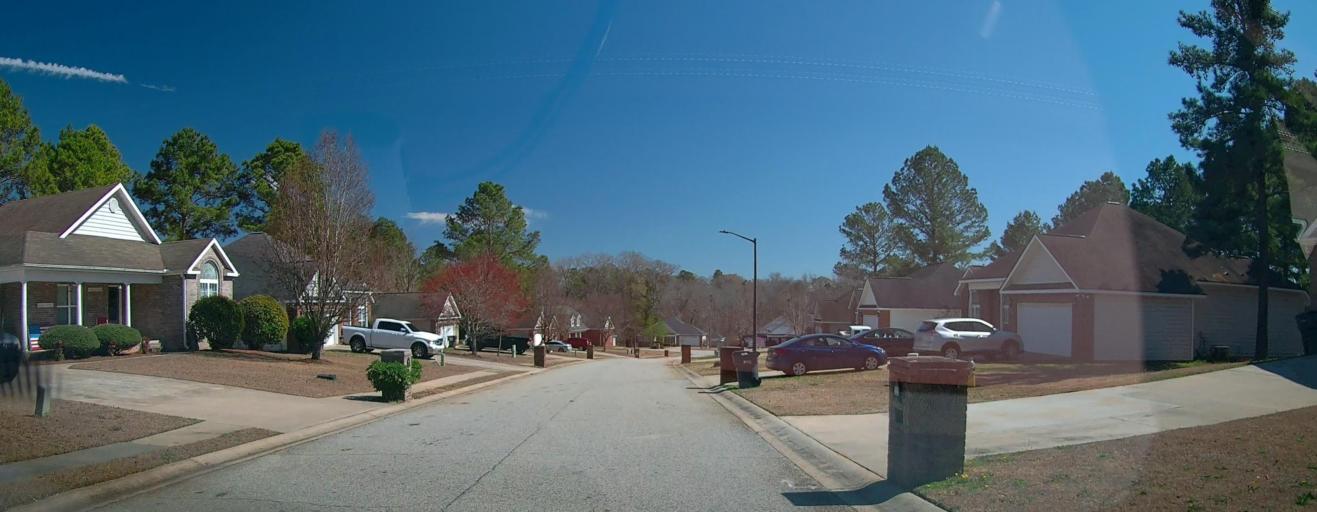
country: US
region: Georgia
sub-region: Houston County
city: Perry
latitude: 32.5016
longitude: -83.6499
